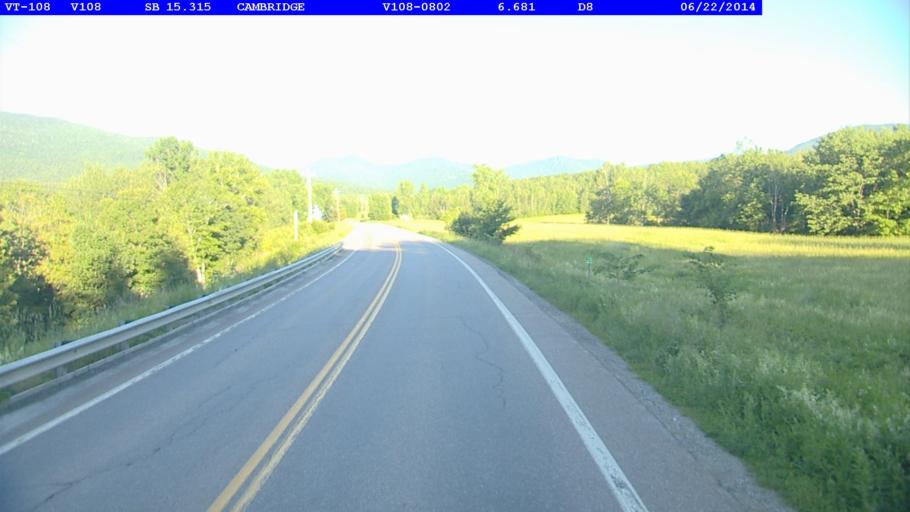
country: US
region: Vermont
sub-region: Lamoille County
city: Johnson
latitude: 44.6176
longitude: -72.8212
